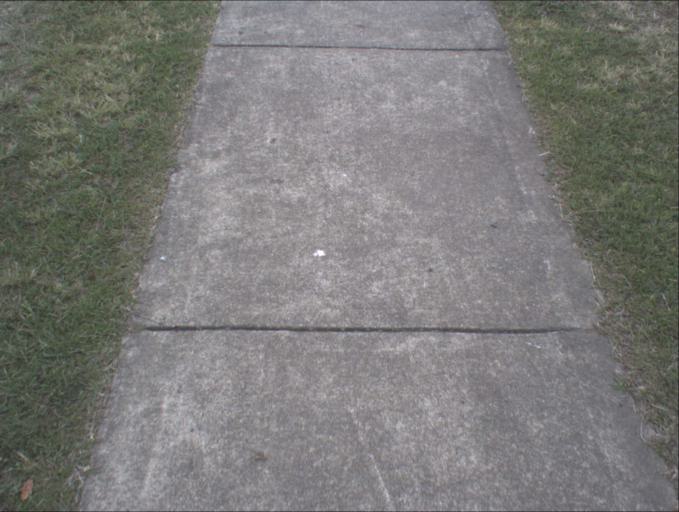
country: AU
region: Queensland
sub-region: Logan
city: Waterford West
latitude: -27.6784
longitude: 153.1367
